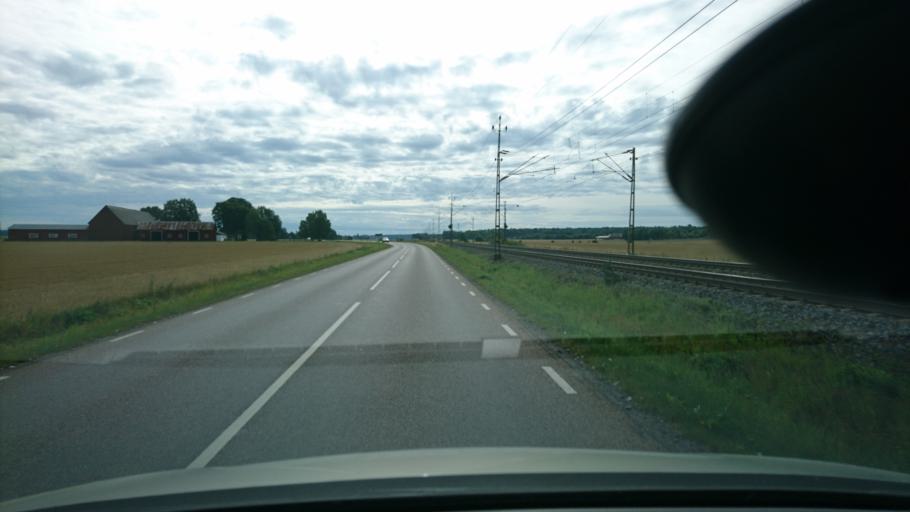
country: SE
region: Uppsala
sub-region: Uppsala Kommun
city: Saevja
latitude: 59.8335
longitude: 17.6943
